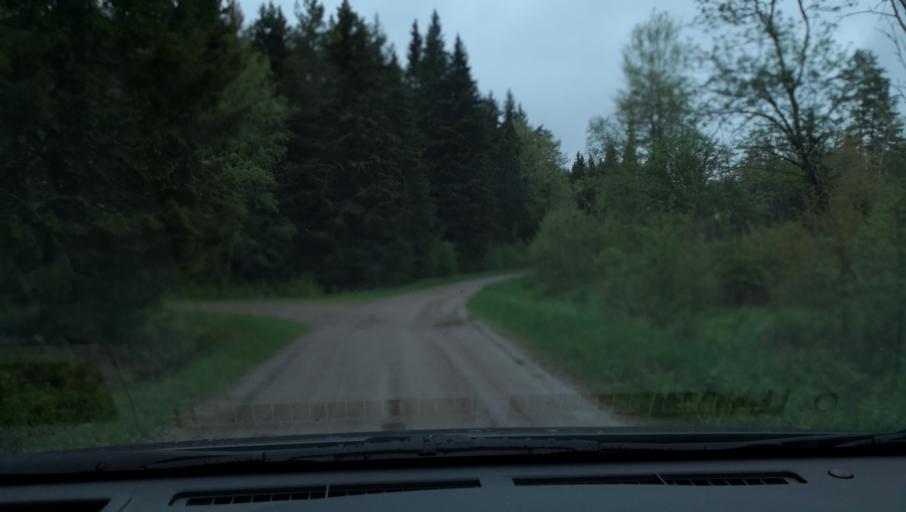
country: SE
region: Uppsala
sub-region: Enkopings Kommun
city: Orsundsbro
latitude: 59.9153
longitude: 17.3487
